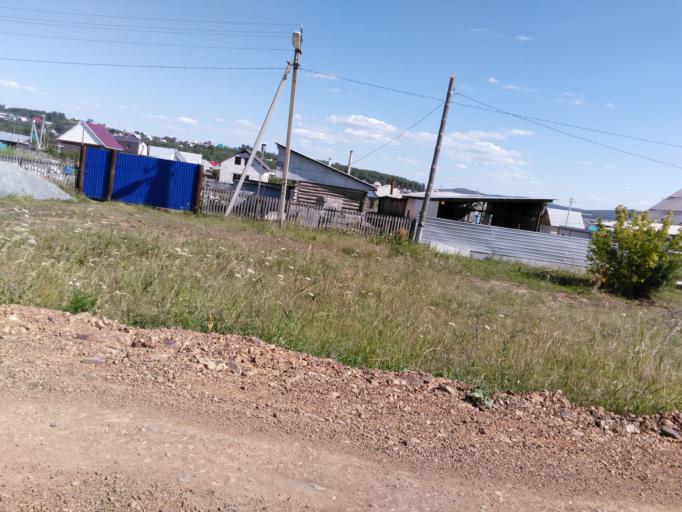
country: RU
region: Bashkortostan
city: Uchaly
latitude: 54.2921
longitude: 59.3600
